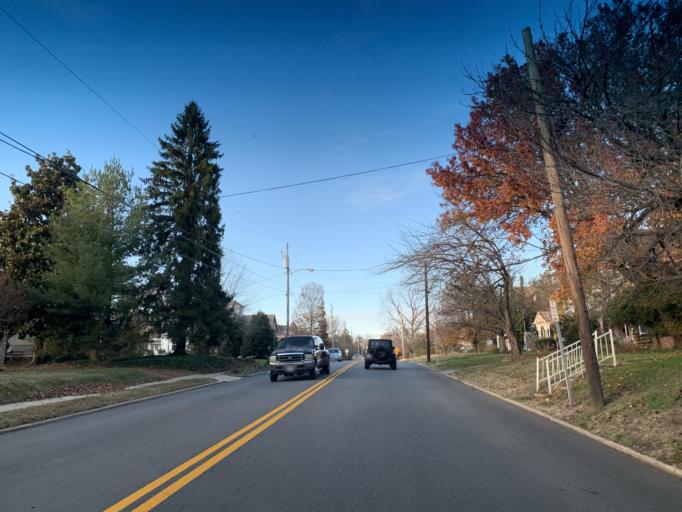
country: US
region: Maryland
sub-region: Kent County
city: Chestertown
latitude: 39.2121
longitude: -76.0660
